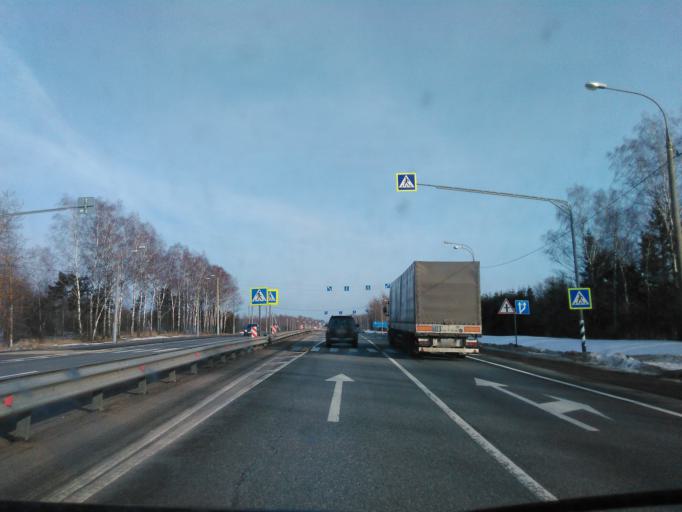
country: RU
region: Smolensk
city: Verkhnedneprovskiy
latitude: 55.1818
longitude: 33.5619
